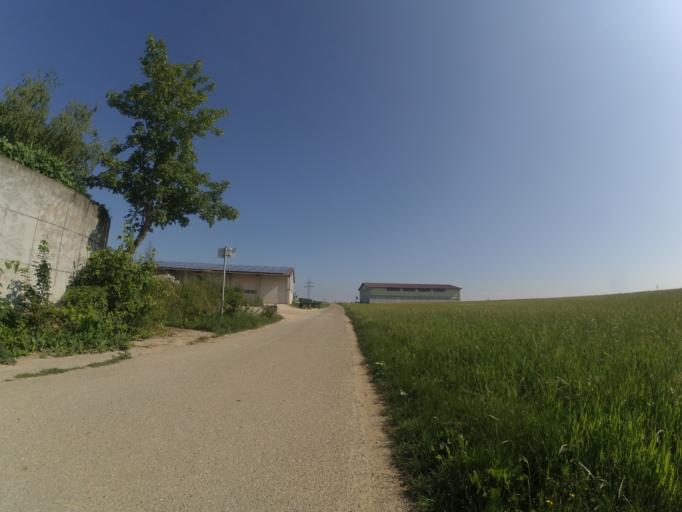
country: DE
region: Baden-Wuerttemberg
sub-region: Tuebingen Region
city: Beimerstetten
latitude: 48.4542
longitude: 9.9893
